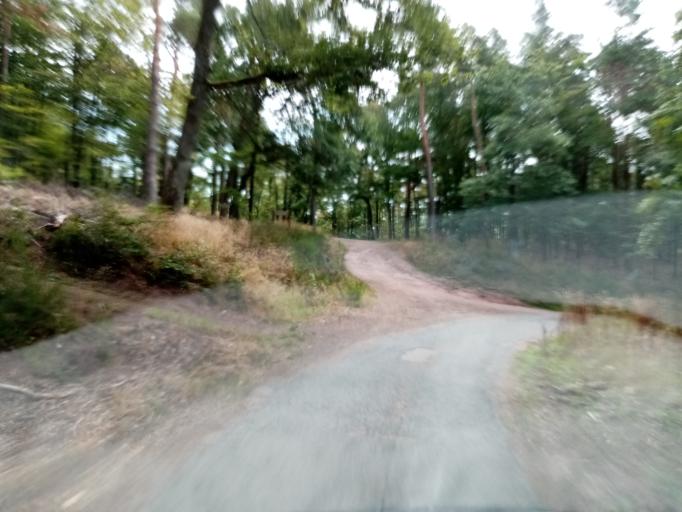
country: FR
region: Alsace
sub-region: Departement du Bas-Rhin
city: Andlau
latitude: 48.3543
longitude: 7.3728
